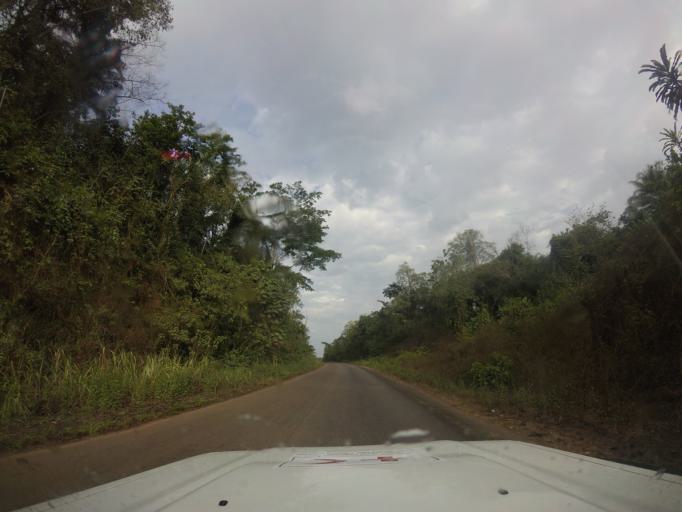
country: LR
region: Bomi
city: Tubmanburg
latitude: 6.7207
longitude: -11.0741
